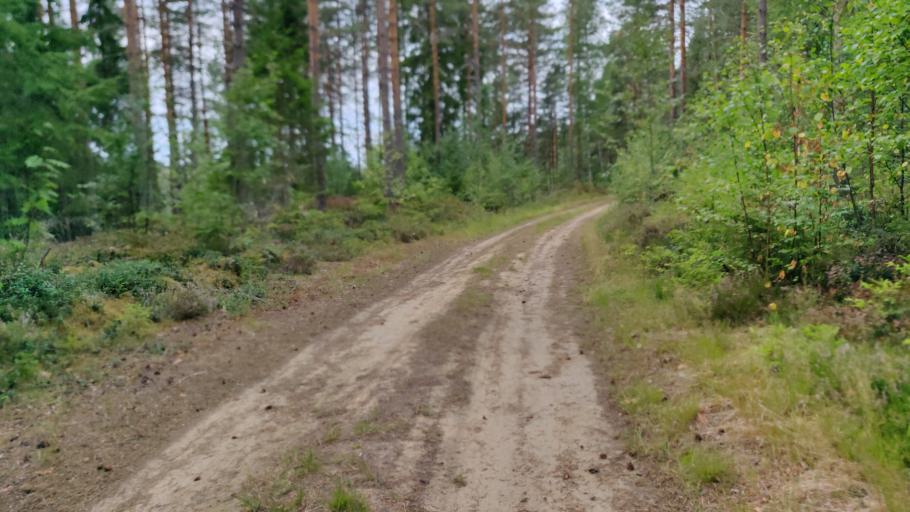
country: SE
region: Vaermland
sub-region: Hagfors Kommun
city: Hagfors
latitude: 60.0148
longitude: 13.5598
